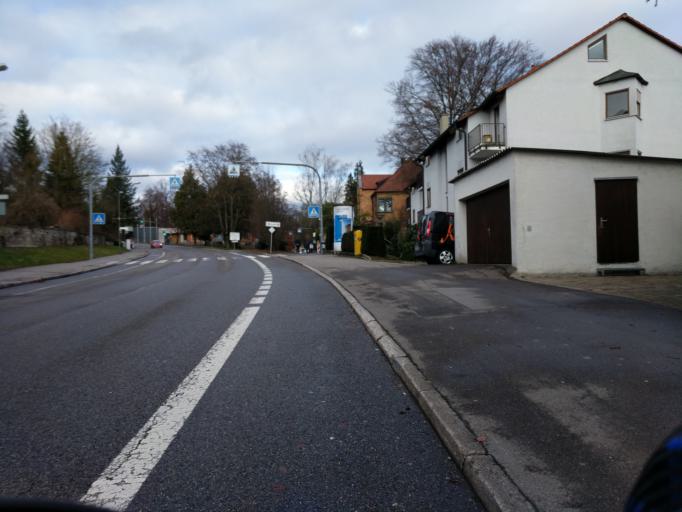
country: DE
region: Baden-Wuerttemberg
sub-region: Tuebingen Region
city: Rottenburg
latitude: 48.4804
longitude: 8.9369
